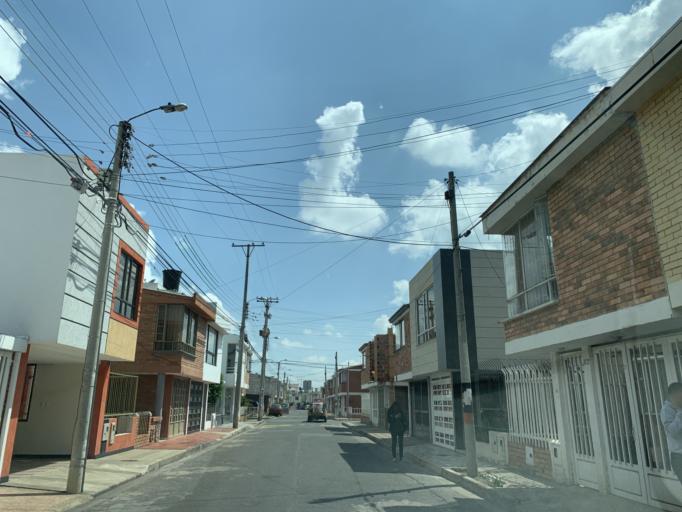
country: CO
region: Boyaca
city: Tunja
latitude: 5.5499
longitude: -73.3512
